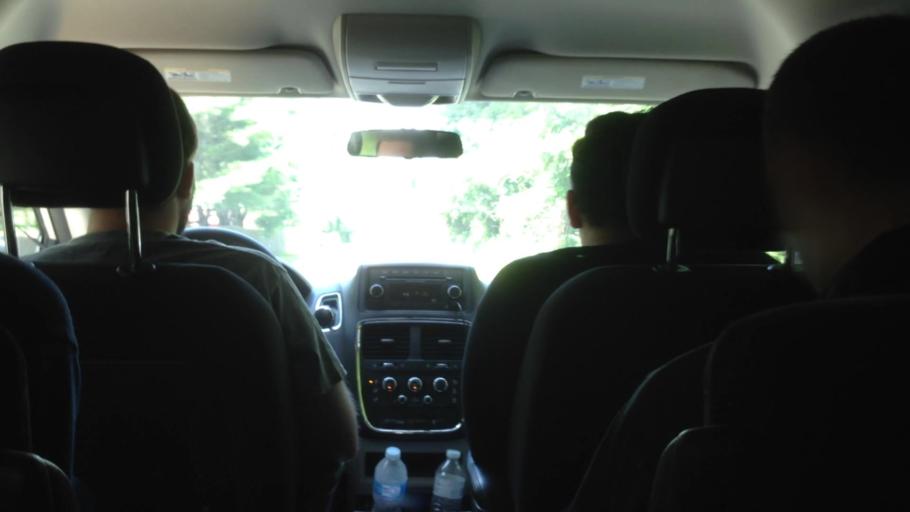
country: US
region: New York
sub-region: Dutchess County
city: Tivoli
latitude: 42.0978
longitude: -73.8962
